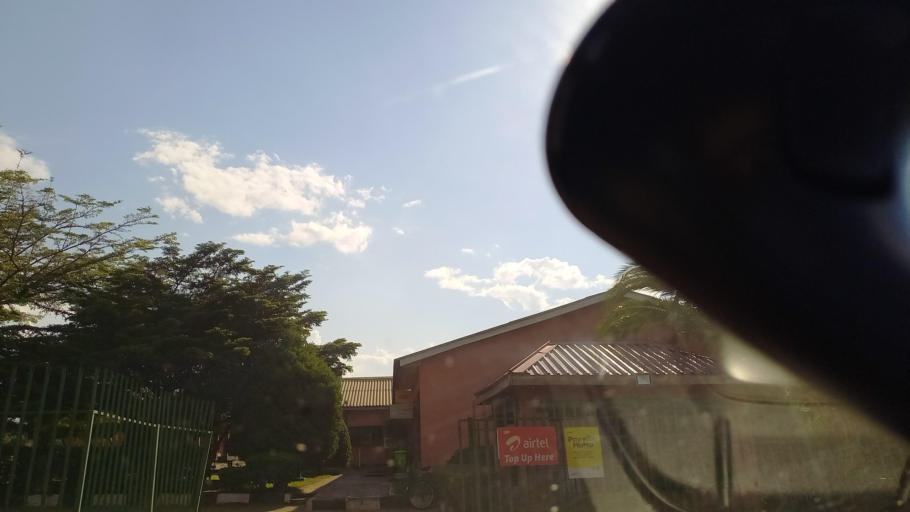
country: ZM
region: Southern
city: Mazabuka
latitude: -15.8633
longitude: 27.7606
